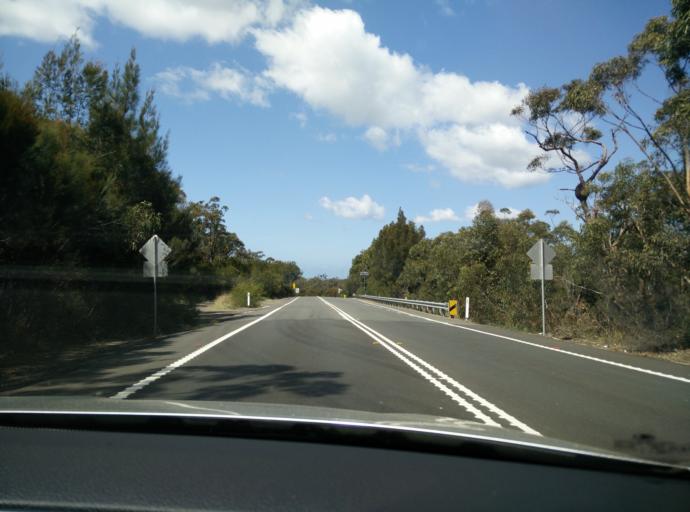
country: AU
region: New South Wales
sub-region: Gosford Shire
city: Blackwall
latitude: -33.4735
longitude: 151.2880
